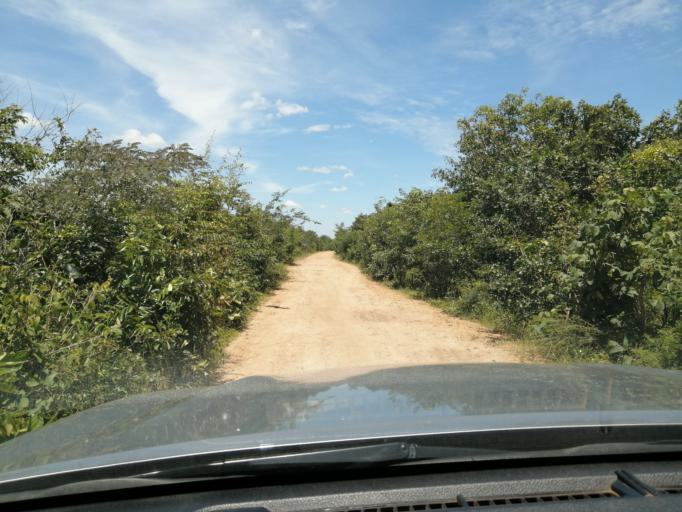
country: ZM
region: Central
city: Chibombo
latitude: -15.0906
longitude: 27.8395
